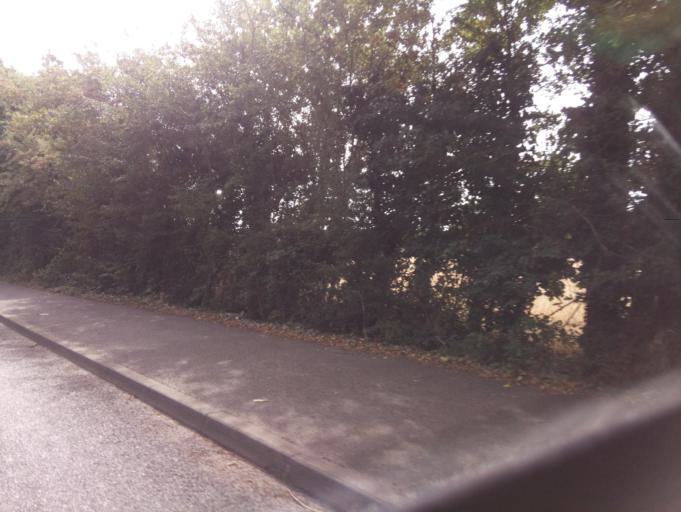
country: GB
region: England
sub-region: Surrey
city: Horley
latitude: 51.1740
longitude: -0.1483
